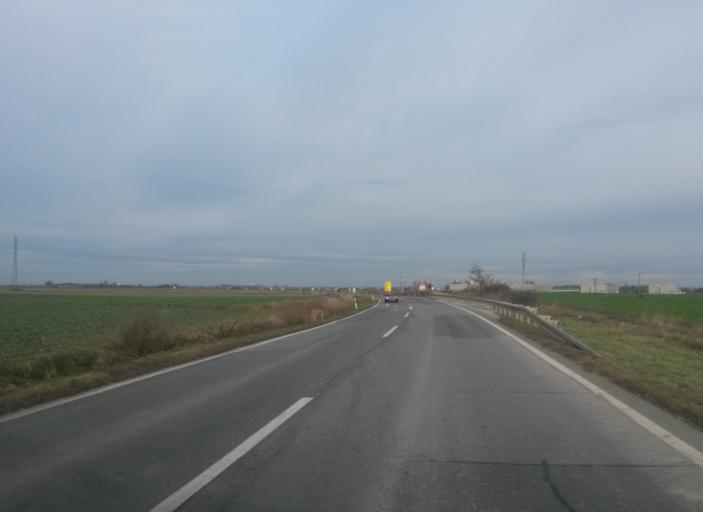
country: HR
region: Osjecko-Baranjska
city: Ovcara
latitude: 45.4930
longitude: 18.5525
